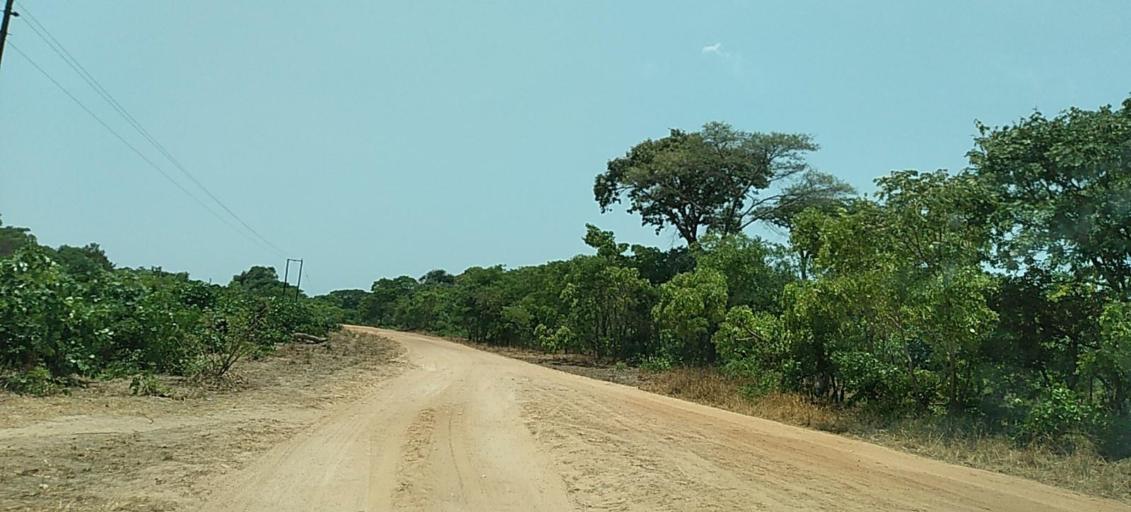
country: ZM
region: Copperbelt
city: Mpongwe
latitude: -13.8099
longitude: 27.8532
